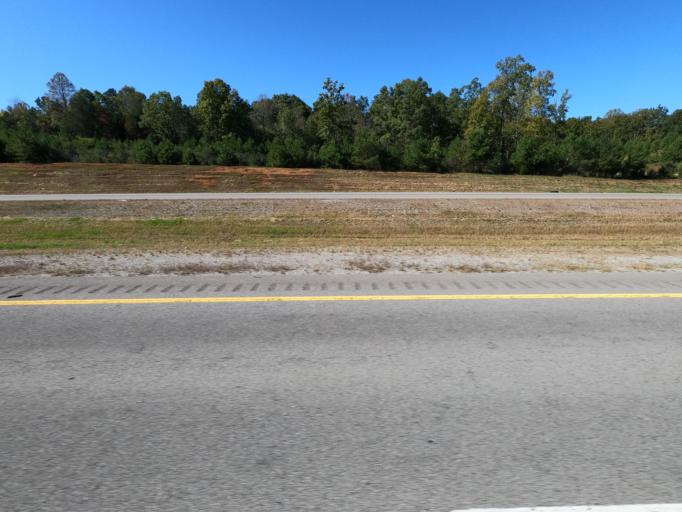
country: US
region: Tennessee
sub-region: Williamson County
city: Fairview
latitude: 35.8678
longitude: -87.0899
